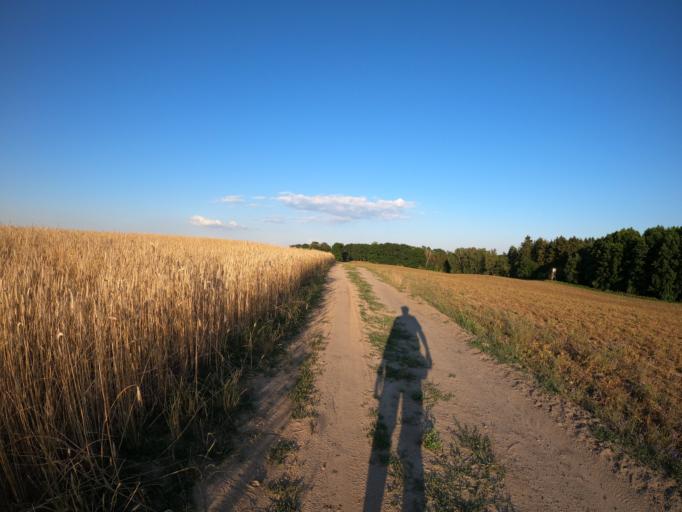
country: DE
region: Brandenburg
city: Althuttendorf
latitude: 53.0265
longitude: 13.8675
